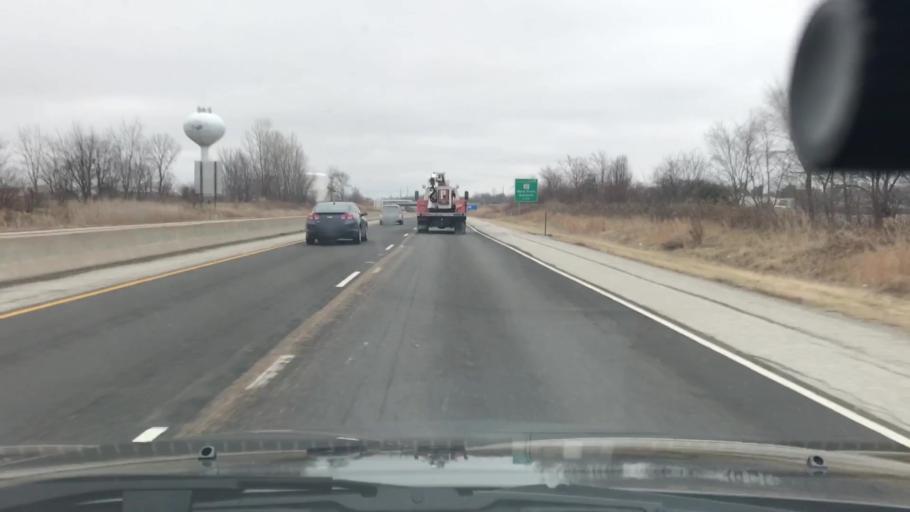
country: US
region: Illinois
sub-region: Madison County
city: Rosewood Heights
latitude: 38.8925
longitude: -90.0628
